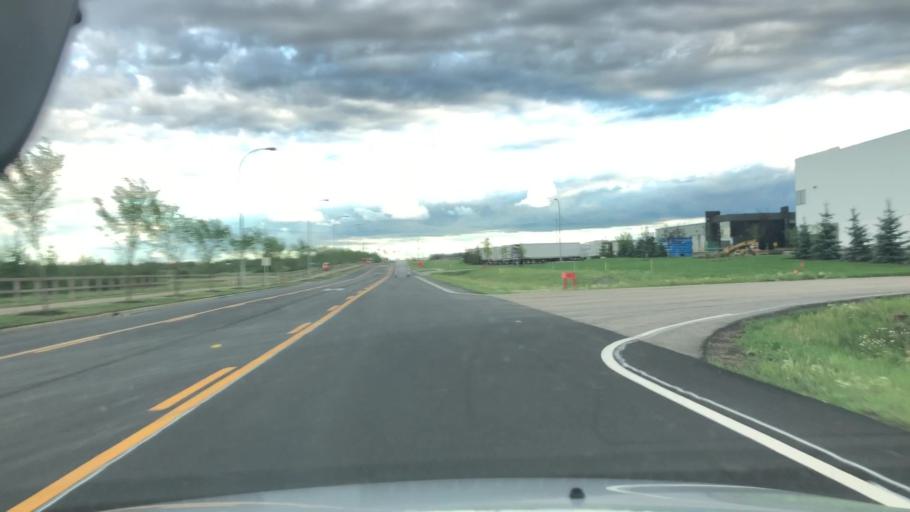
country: CA
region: Alberta
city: St. Albert
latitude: 53.6183
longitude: -113.5698
